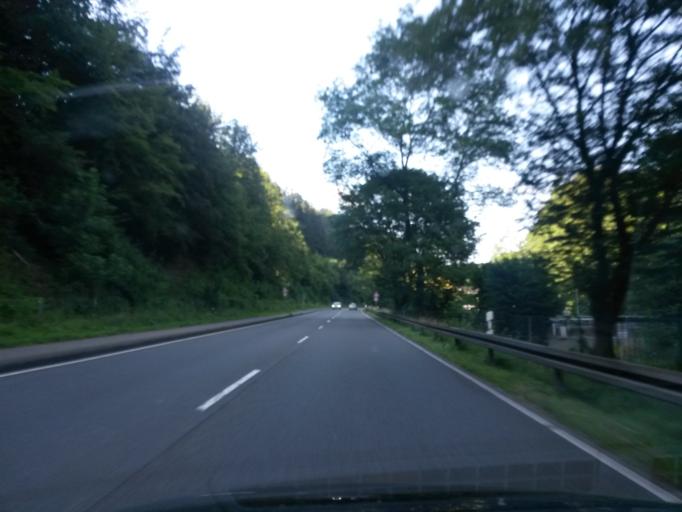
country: DE
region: North Rhine-Westphalia
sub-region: Regierungsbezirk Koln
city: Gummersbach
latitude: 50.9986
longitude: 7.5513
